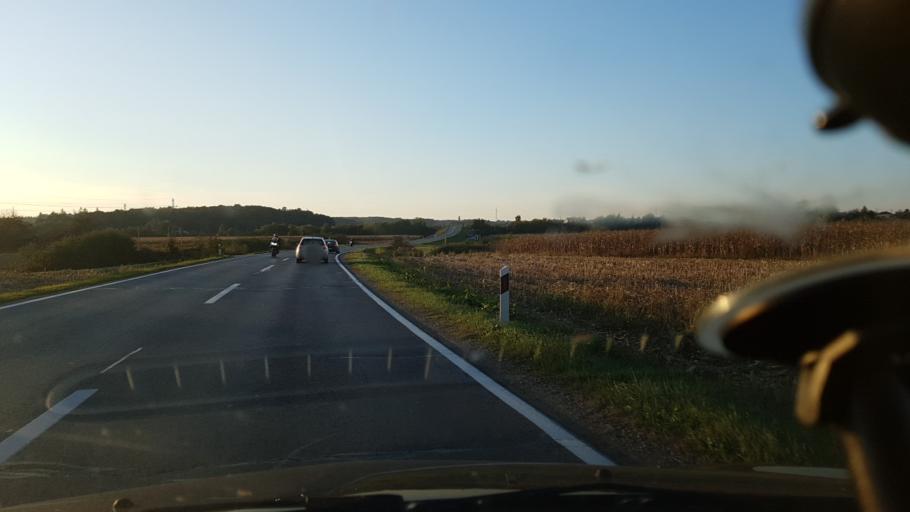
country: HR
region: Koprivnicko-Krizevacka
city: Stari Grad
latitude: 46.1499
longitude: 16.8126
